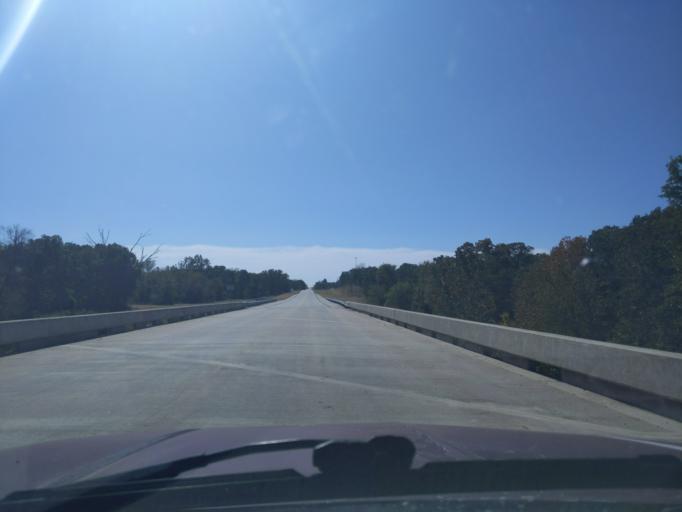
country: US
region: Oklahoma
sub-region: Creek County
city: Bristow
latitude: 35.7359
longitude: -96.3872
